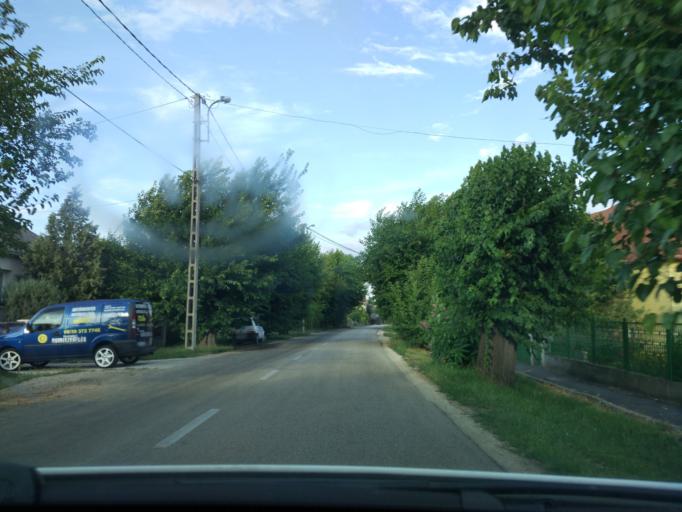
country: HU
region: Veszprem
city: Varpalota
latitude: 47.2003
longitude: 18.1725
